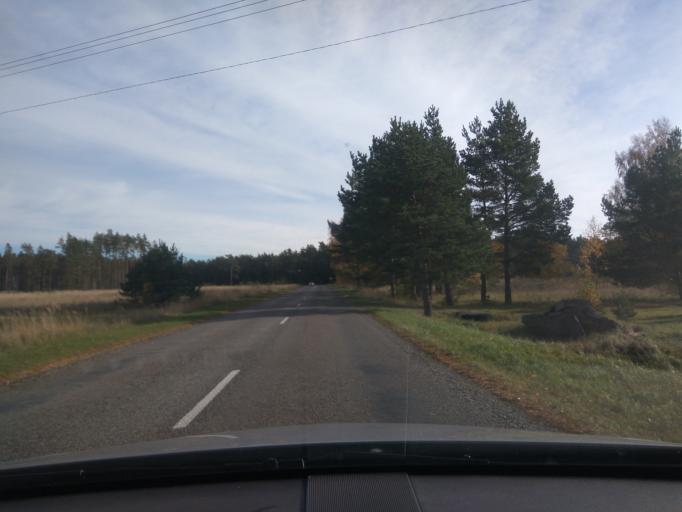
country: LV
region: Alsunga
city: Alsunga
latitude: 57.0112
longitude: 21.3959
